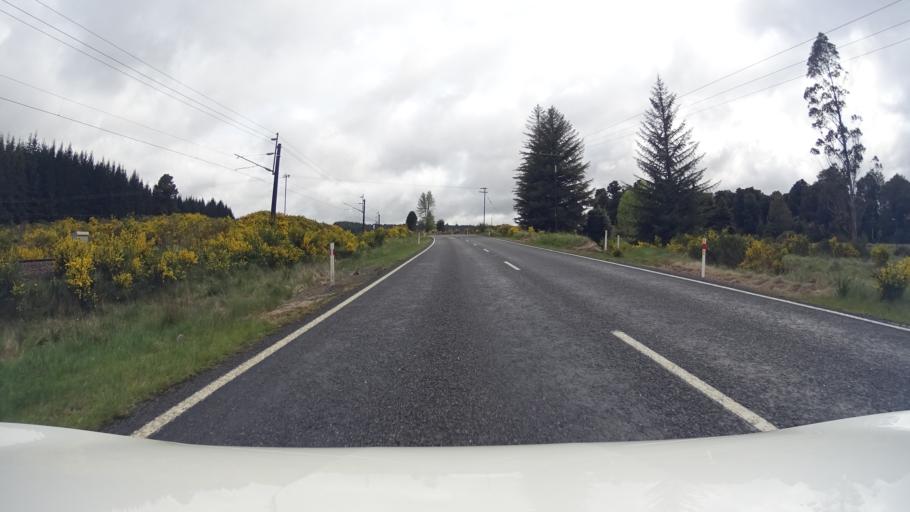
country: NZ
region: Manawatu-Wanganui
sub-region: Ruapehu District
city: Waiouru
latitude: -39.2112
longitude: 175.4018
